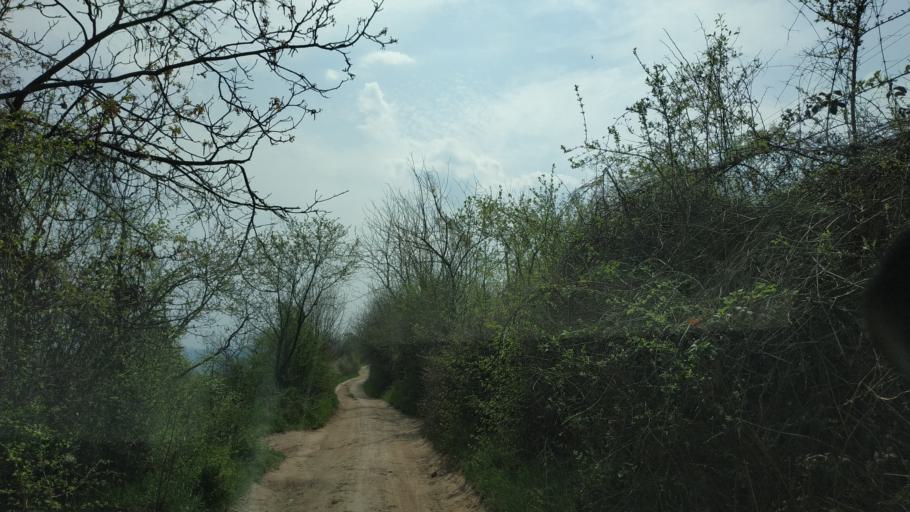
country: RS
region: Central Serbia
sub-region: Nisavski Okrug
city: Aleksinac
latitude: 43.5406
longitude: 21.7261
